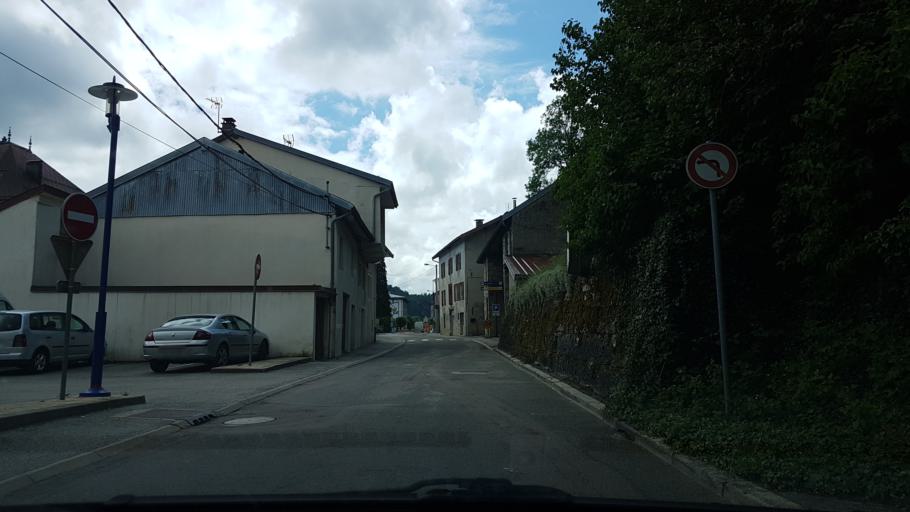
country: FR
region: Franche-Comte
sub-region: Departement du Jura
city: Moirans-en-Montagne
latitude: 46.4319
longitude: 5.7245
